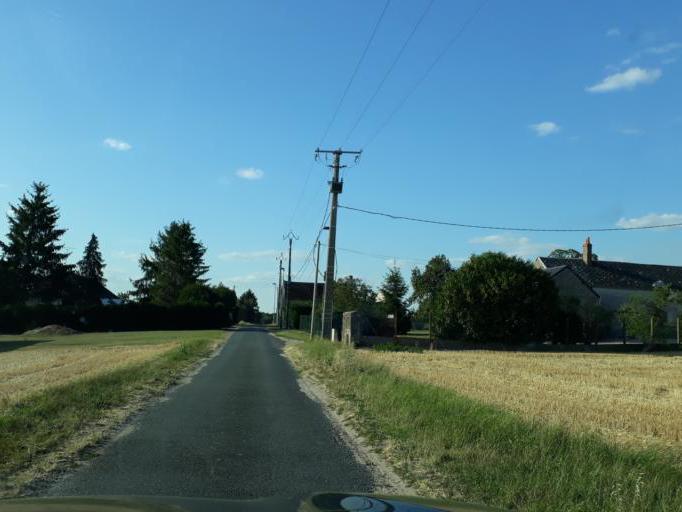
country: FR
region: Centre
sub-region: Departement du Loiret
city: Chaingy
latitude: 47.9013
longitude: 1.7592
